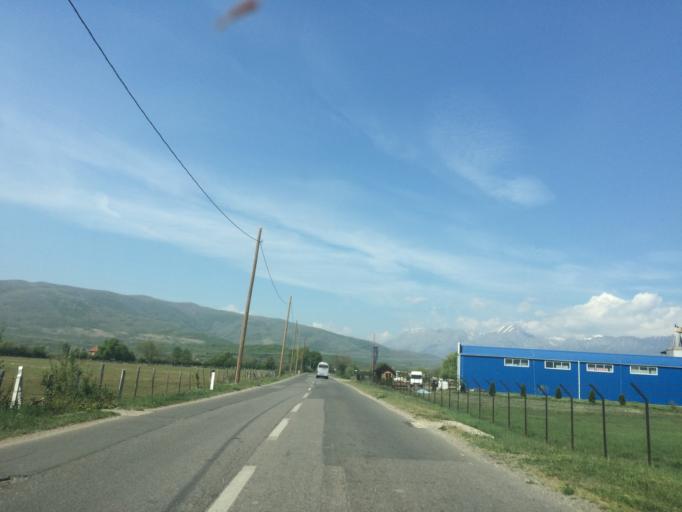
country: XK
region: Gjakova
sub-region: Komuna e Gjakoves
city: Gjakove
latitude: 42.3757
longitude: 20.3377
